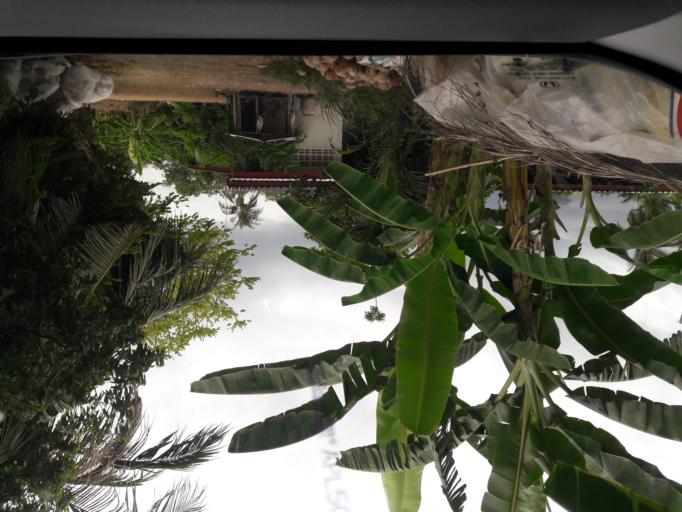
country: TH
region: Ratchaburi
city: Damnoen Saduak
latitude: 13.5583
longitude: 99.9860
